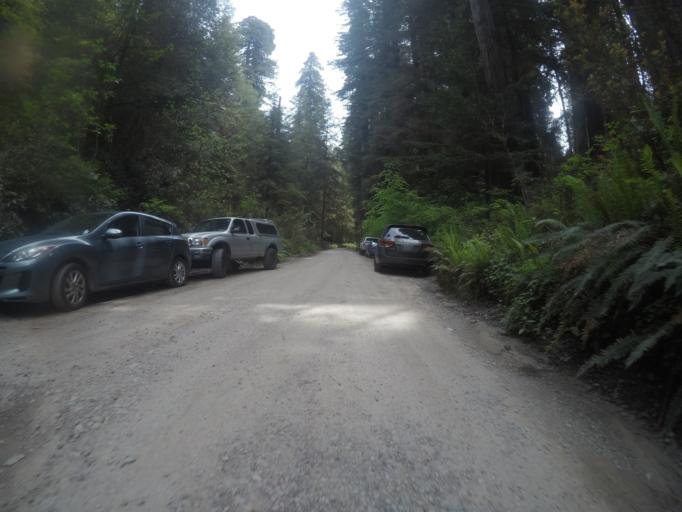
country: US
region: California
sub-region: Del Norte County
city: Bertsch-Oceanview
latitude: 41.7688
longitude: -124.1096
